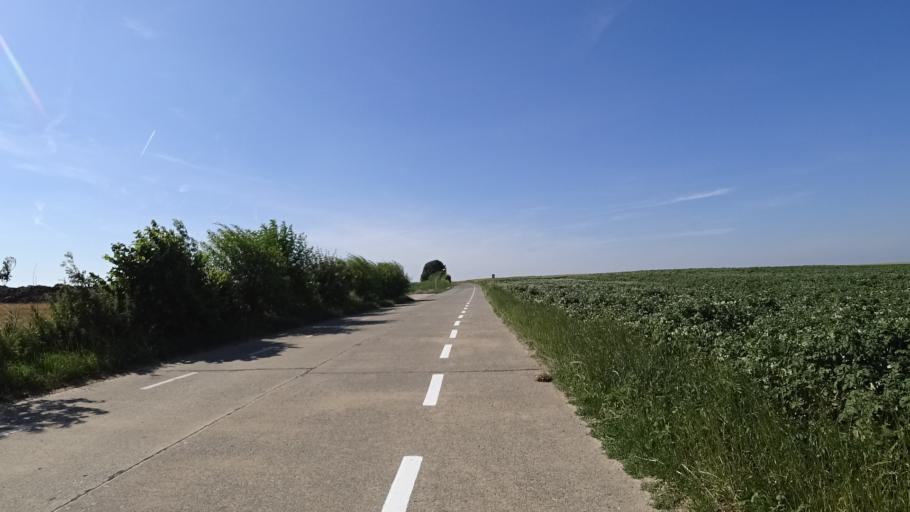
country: BE
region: Wallonia
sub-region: Province du Brabant Wallon
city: Incourt
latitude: 50.6645
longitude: 4.8111
